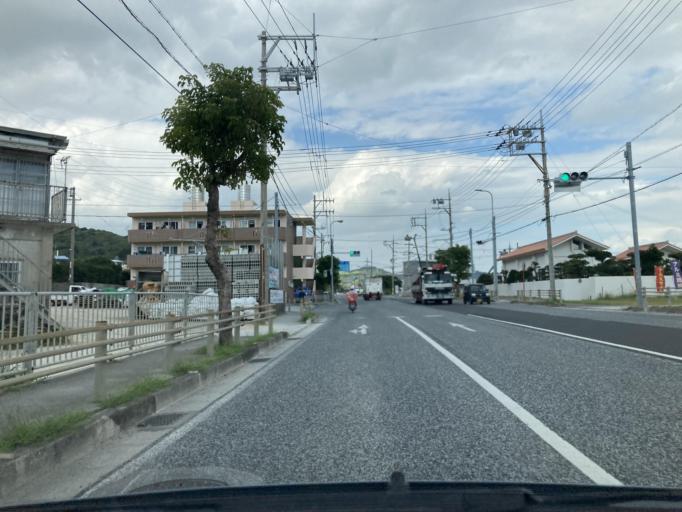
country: JP
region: Okinawa
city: Ginowan
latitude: 26.2536
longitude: 127.7842
